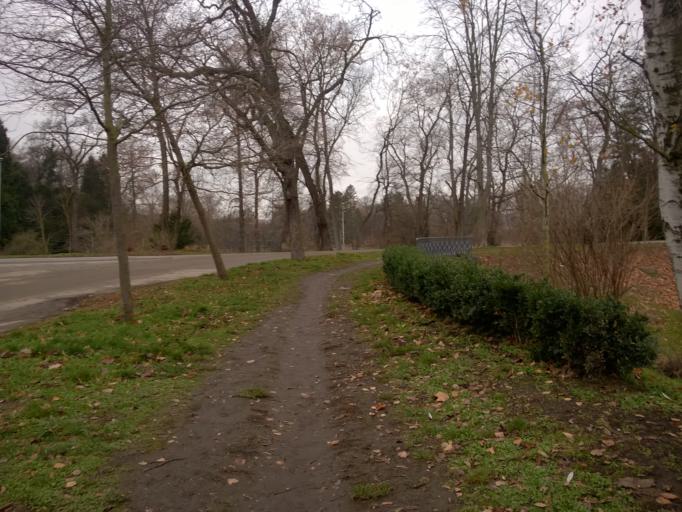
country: CZ
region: Praha
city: Prague
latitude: 50.1054
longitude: 14.4160
